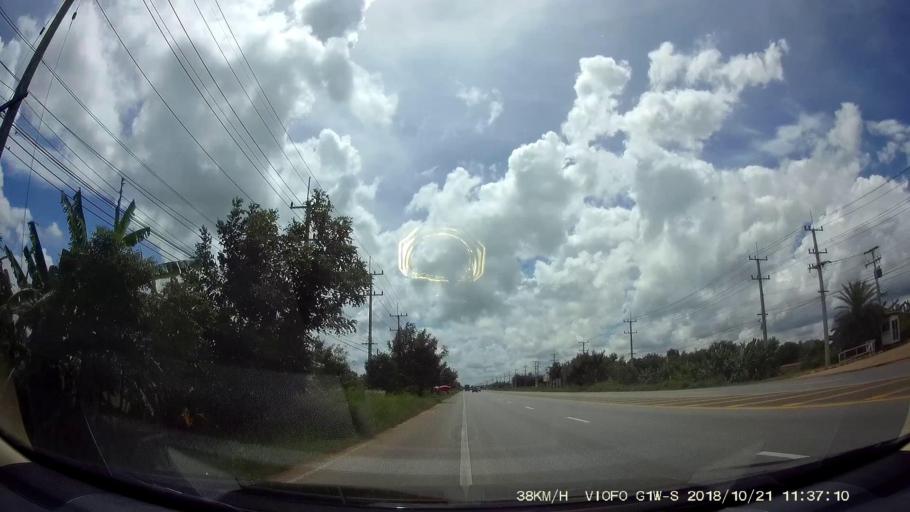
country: TH
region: Chaiyaphum
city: Chaiyaphum
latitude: 15.7167
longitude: 102.0161
